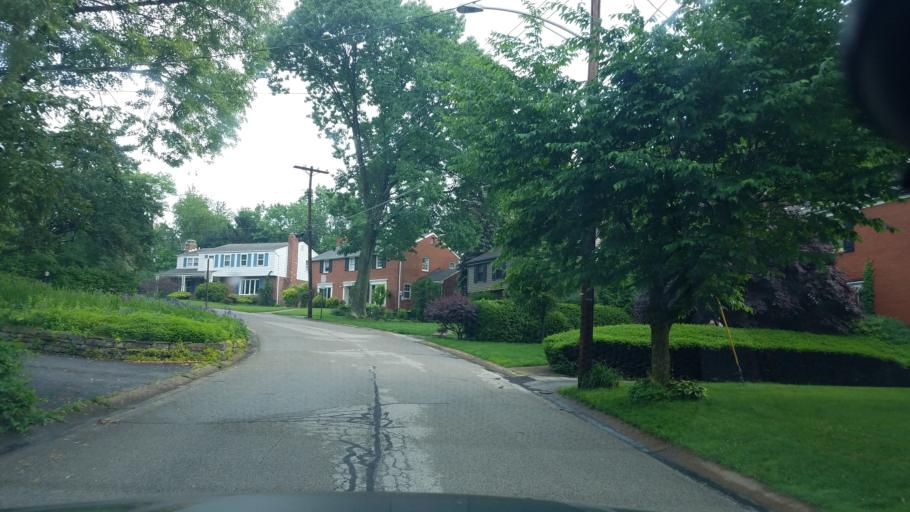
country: US
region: Pennsylvania
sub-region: Allegheny County
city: Edgewood
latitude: 40.4341
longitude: -79.8746
